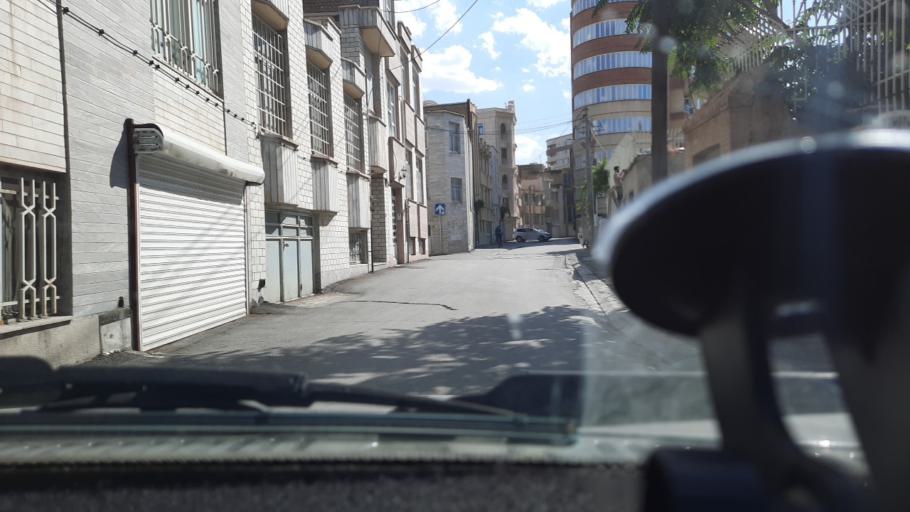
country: IR
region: Markazi
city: Arak
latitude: 34.0824
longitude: 49.6914
